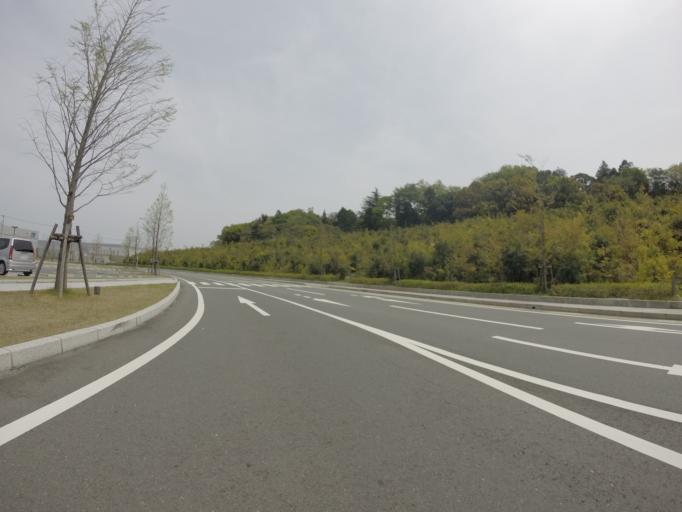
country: JP
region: Shizuoka
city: Kakegawa
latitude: 34.7573
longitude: 137.9990
